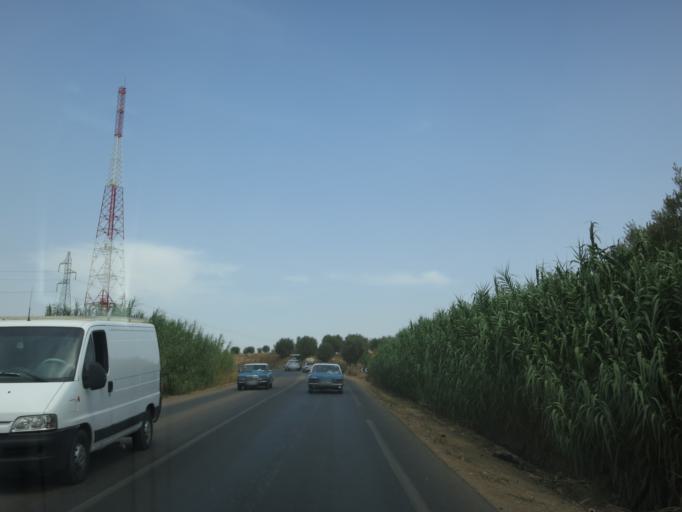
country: MA
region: Meknes-Tafilalet
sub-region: Meknes
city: Meknes
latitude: 33.9643
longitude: -5.5751
